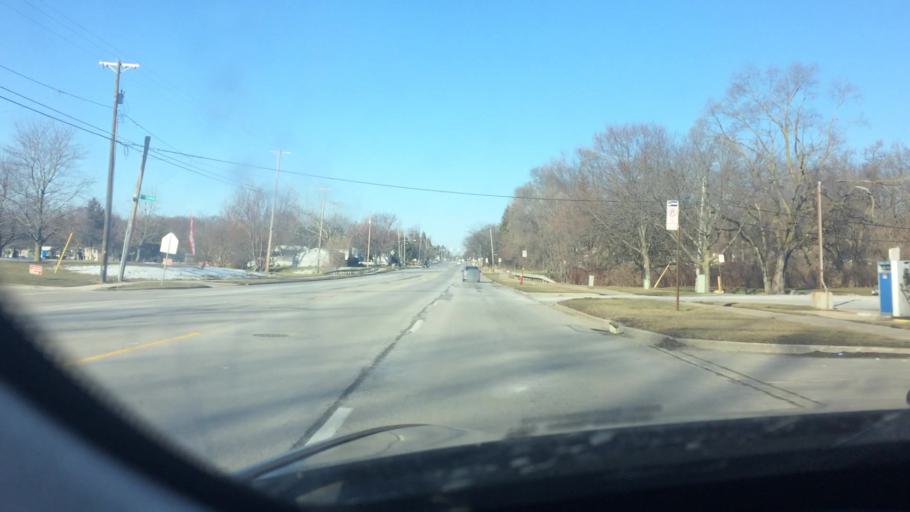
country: US
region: Ohio
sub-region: Lucas County
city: Ottawa Hills
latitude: 41.6383
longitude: -83.6349
